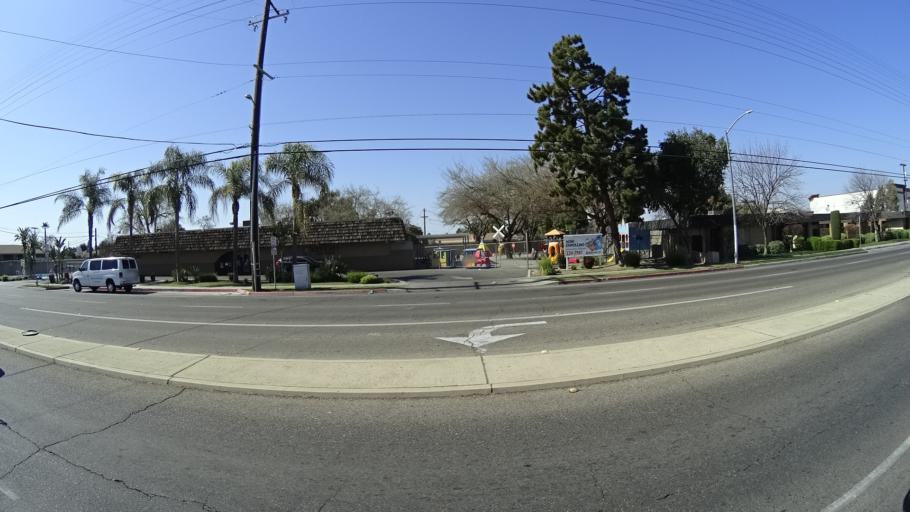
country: US
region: California
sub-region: Fresno County
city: Fresno
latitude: 36.7776
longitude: -119.8265
